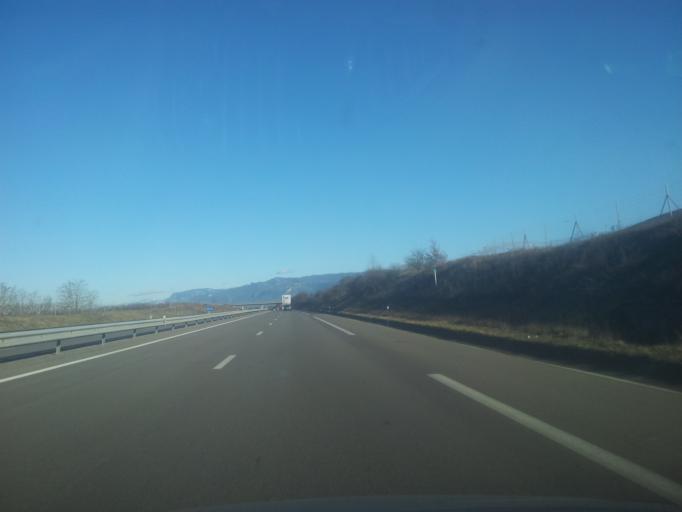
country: FR
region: Rhone-Alpes
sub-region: Departement de la Drome
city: Saint-Paul-les-Romans
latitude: 45.0501
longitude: 5.1725
